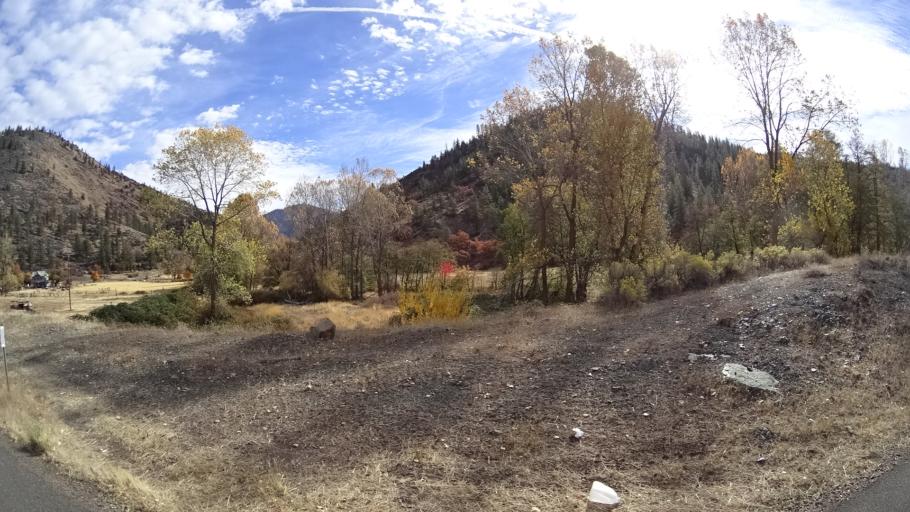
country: US
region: California
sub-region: Siskiyou County
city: Yreka
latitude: 41.6336
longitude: -122.7521
